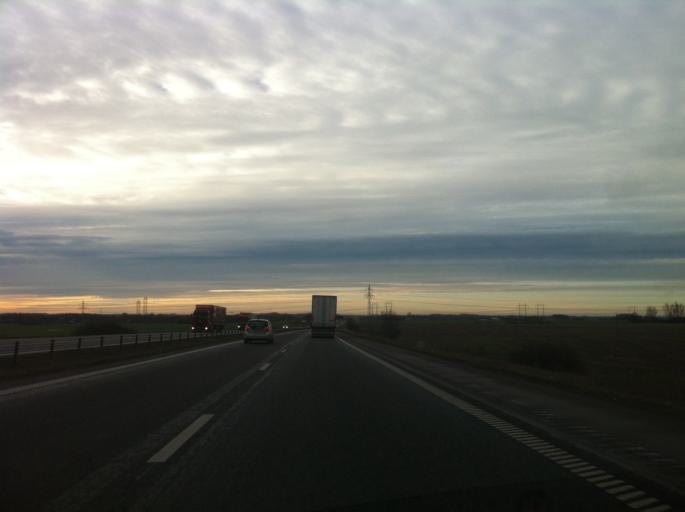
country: SE
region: Skane
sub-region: Helsingborg
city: Hyllinge
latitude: 56.1165
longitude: 12.8871
